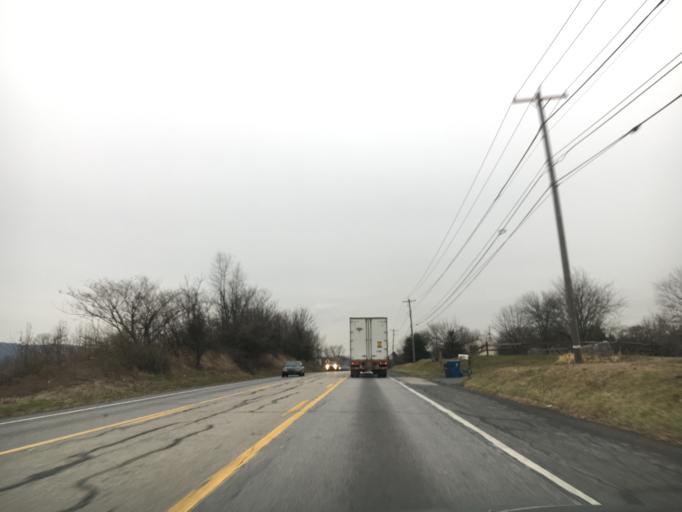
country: US
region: Pennsylvania
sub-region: Berks County
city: Blandon
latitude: 40.4596
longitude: -75.8770
